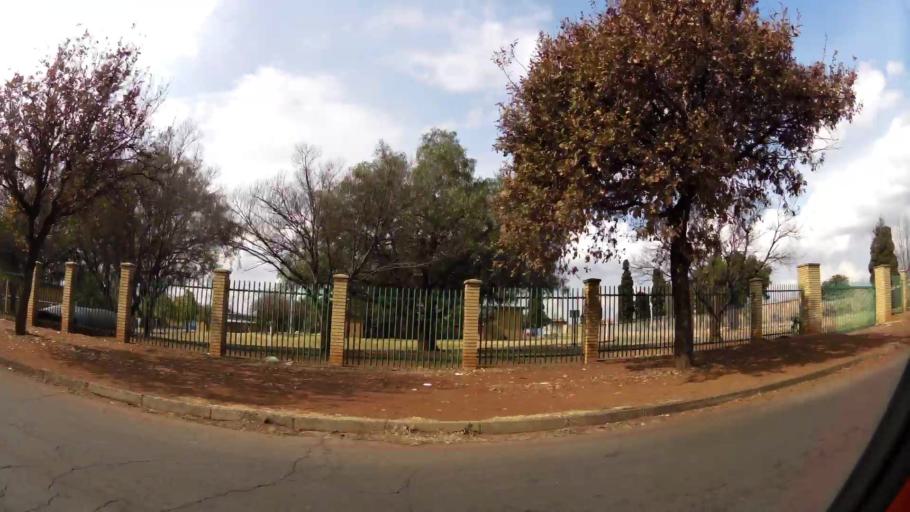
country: ZA
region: Gauteng
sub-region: Sedibeng District Municipality
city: Vanderbijlpark
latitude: -26.7174
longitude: 27.8633
